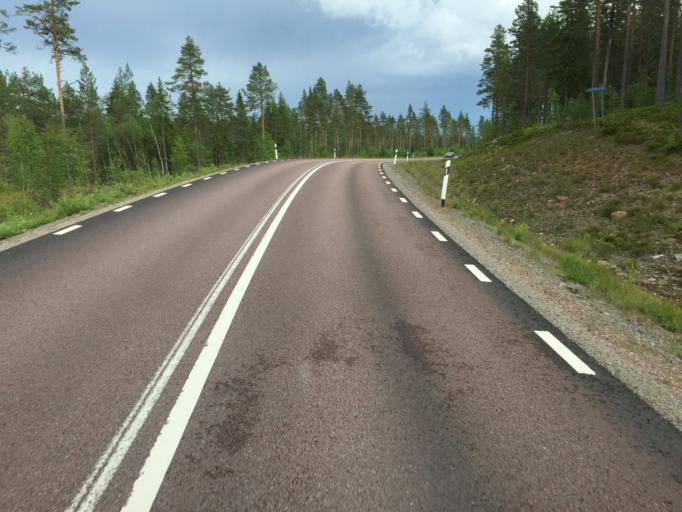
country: SE
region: Dalarna
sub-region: Vansbro Kommun
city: Vansbro
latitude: 60.8195
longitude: 14.0935
